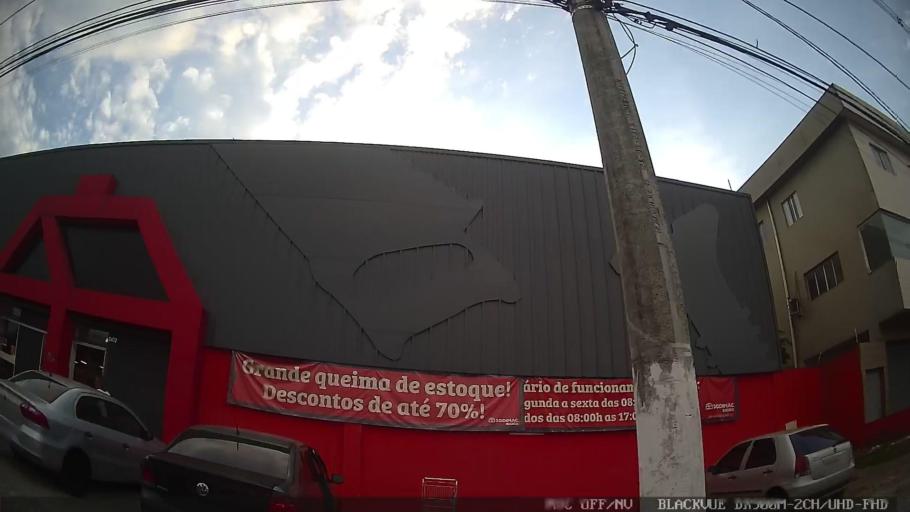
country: BR
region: Sao Paulo
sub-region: Cubatao
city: Cubatao
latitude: -23.8963
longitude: -46.4214
